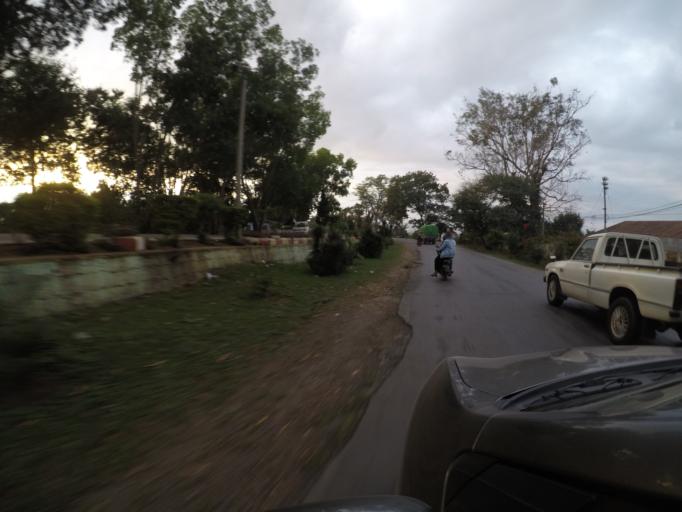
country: MM
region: Shan
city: Taunggyi
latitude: 20.7920
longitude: 97.0149
